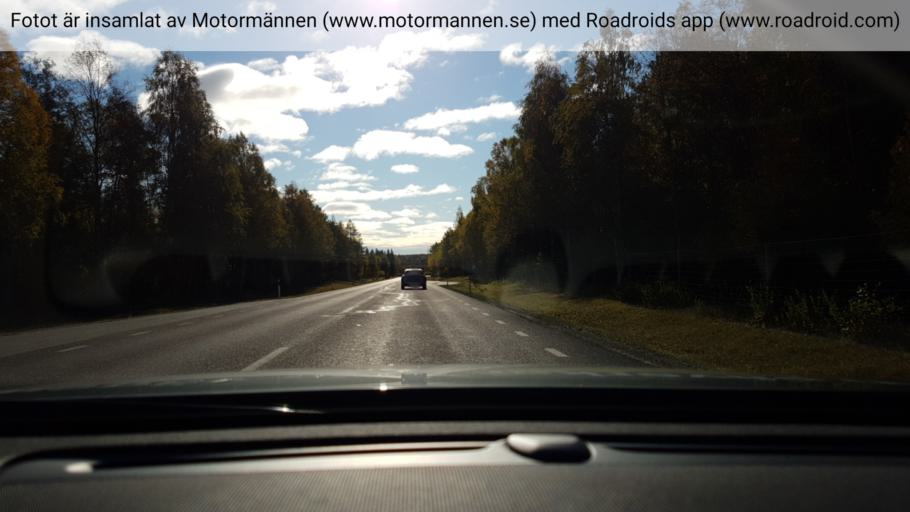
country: SE
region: Vaesterbotten
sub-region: Skelleftea Kommun
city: Burea
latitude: 64.4102
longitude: 21.2955
